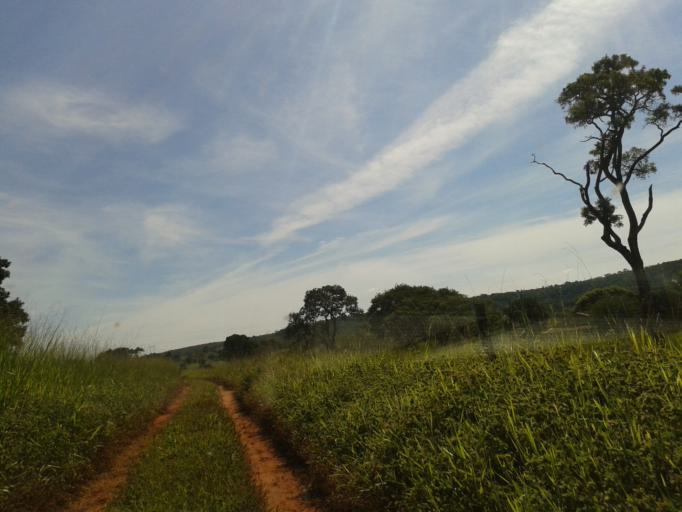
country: BR
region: Minas Gerais
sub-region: Campina Verde
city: Campina Verde
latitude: -19.4350
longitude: -49.6963
